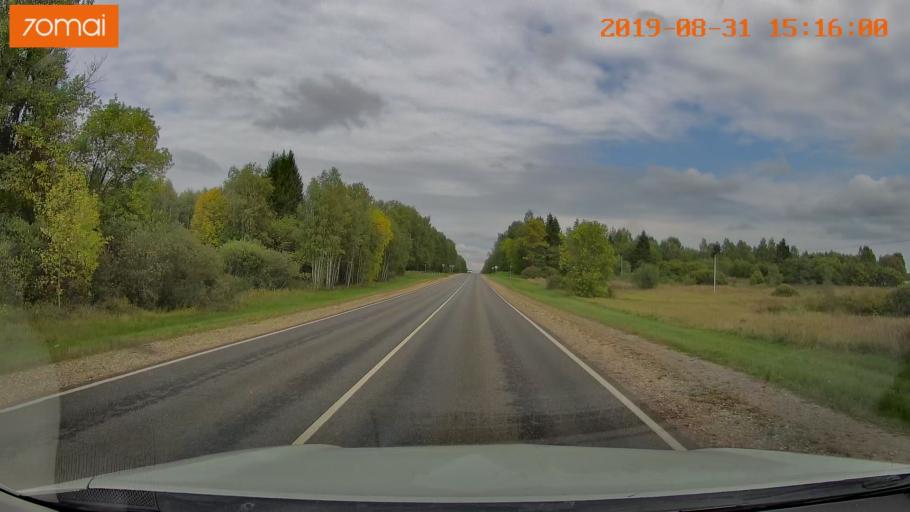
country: RU
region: Kaluga
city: Baryatino
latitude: 54.4562
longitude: 34.3397
